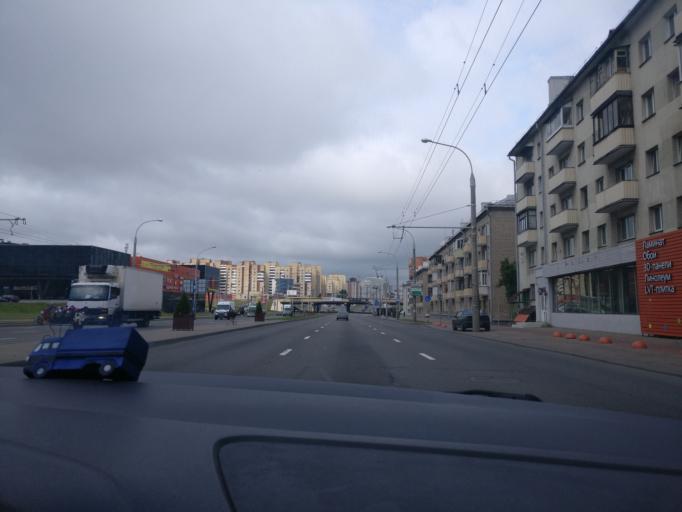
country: BY
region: Minsk
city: Minsk
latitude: 53.8731
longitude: 27.5751
